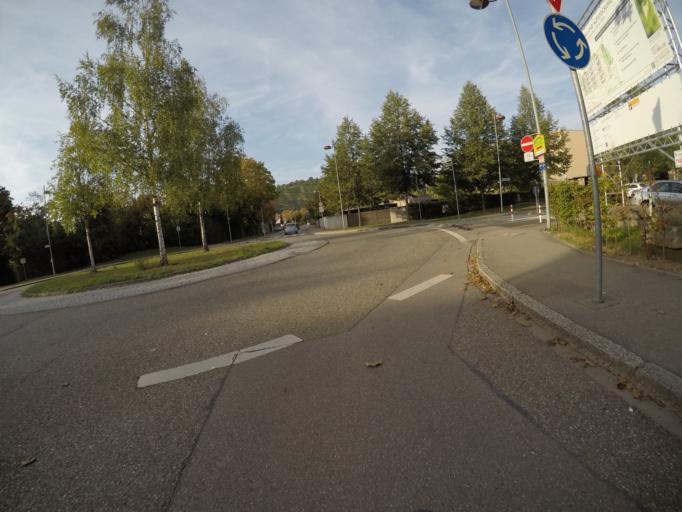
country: DE
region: Baden-Wuerttemberg
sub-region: Regierungsbezirk Stuttgart
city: Esslingen
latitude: 48.7355
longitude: 9.2901
